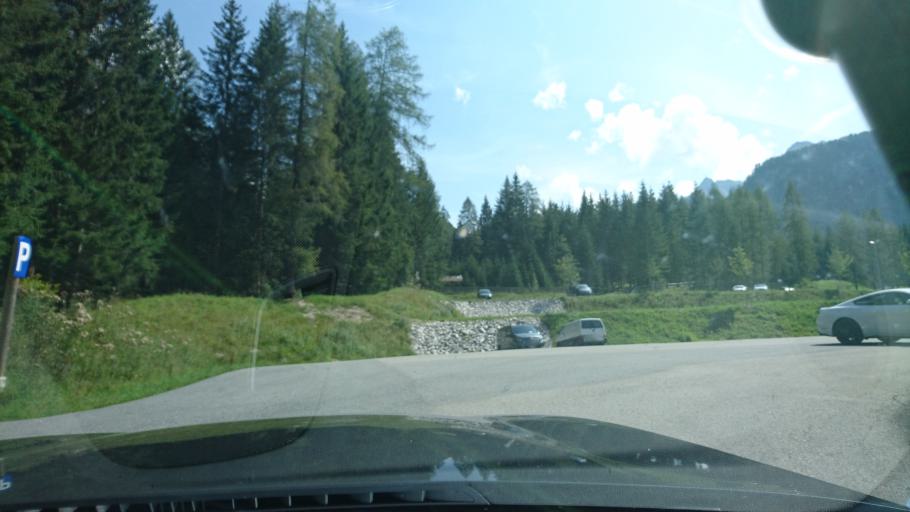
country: AT
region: Tyrol
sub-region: Politischer Bezirk Reutte
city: Ehrwald
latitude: 47.3889
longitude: 10.9387
